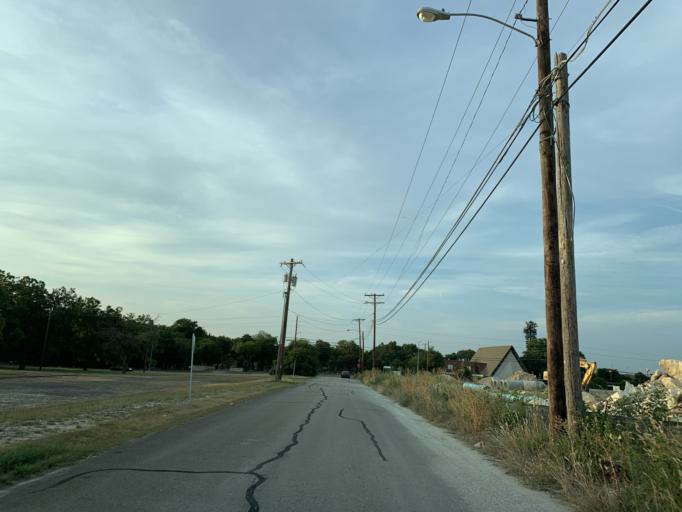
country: US
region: Texas
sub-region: Dallas County
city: Cockrell Hill
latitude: 32.7046
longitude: -96.8829
